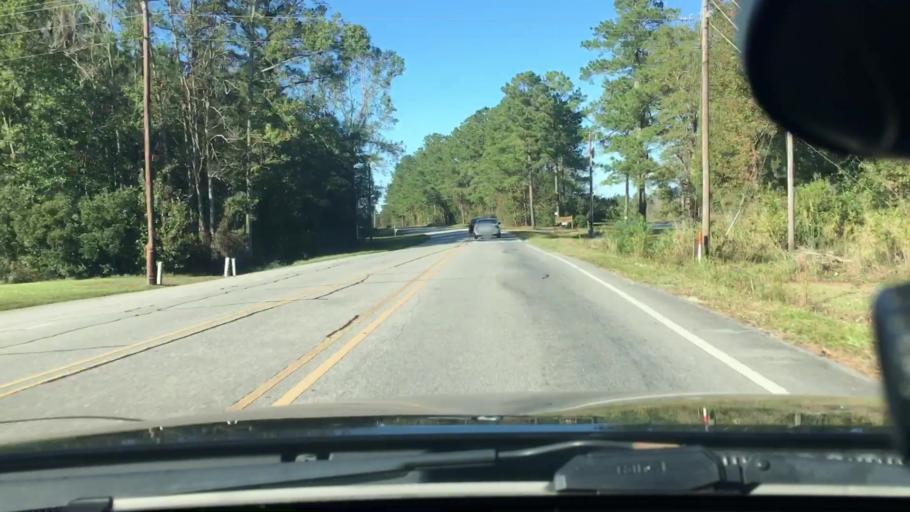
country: US
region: North Carolina
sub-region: Craven County
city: Vanceboro
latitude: 35.2386
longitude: -77.1352
